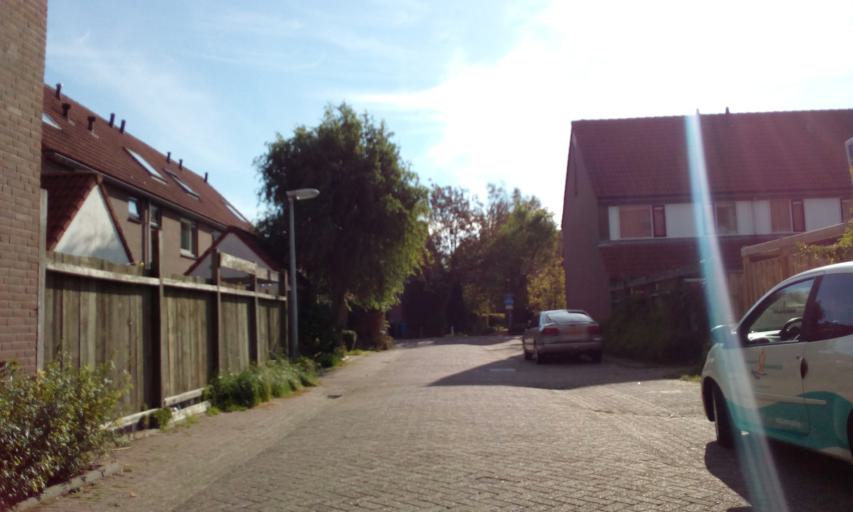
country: NL
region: South Holland
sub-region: Gemeente Leidschendam-Voorburg
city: Voorburg
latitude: 52.0916
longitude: 4.4035
